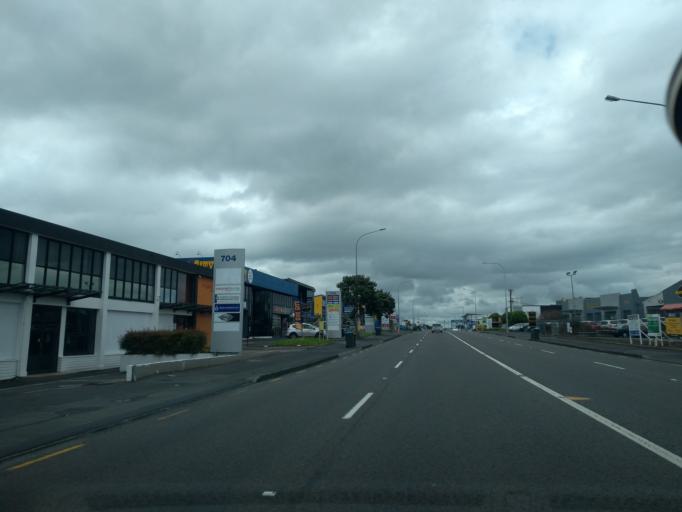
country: NZ
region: Auckland
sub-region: Auckland
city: Tamaki
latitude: -36.9048
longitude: 174.8095
